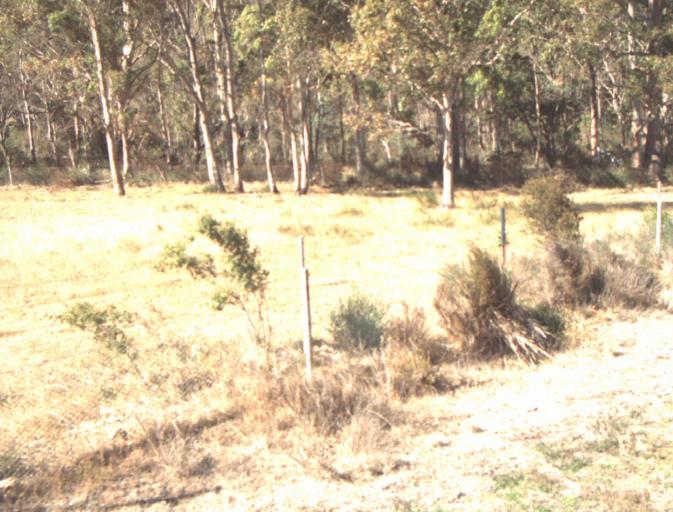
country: AU
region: Tasmania
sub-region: Launceston
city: Newstead
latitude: -41.3163
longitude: 147.3307
